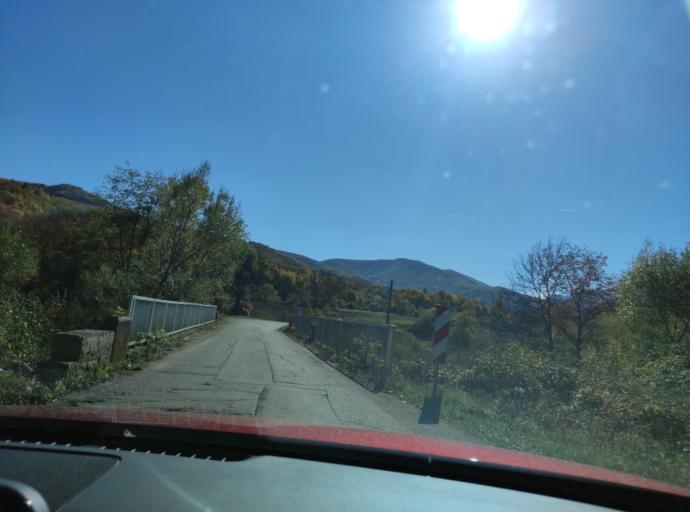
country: BG
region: Montana
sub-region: Obshtina Chiprovtsi
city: Chiprovtsi
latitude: 43.3968
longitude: 22.9253
